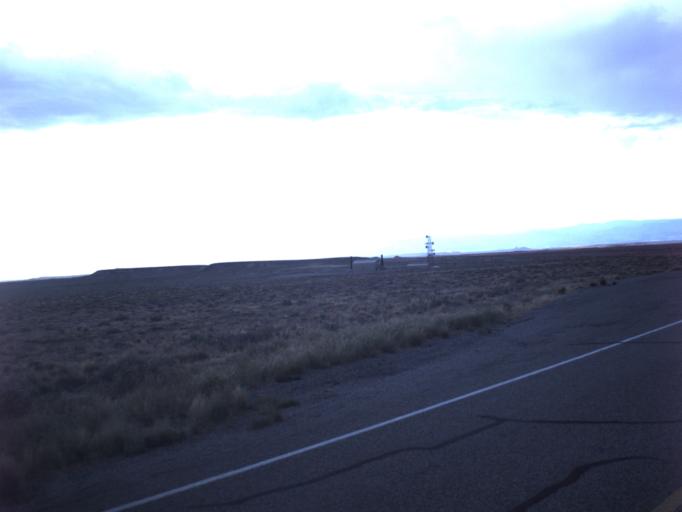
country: US
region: Utah
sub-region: Grand County
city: Moab
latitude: 38.9299
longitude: -109.3429
